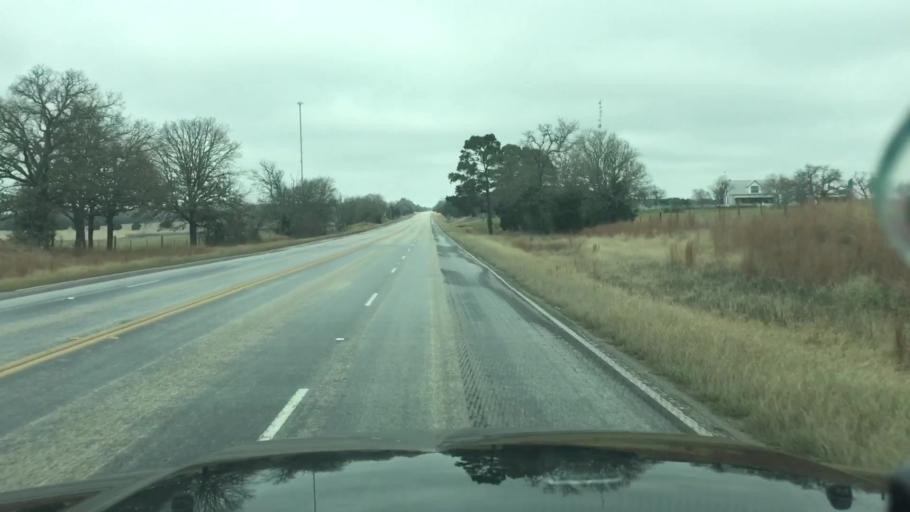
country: US
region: Texas
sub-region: Lee County
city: Giddings
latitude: 30.1026
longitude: -96.9139
